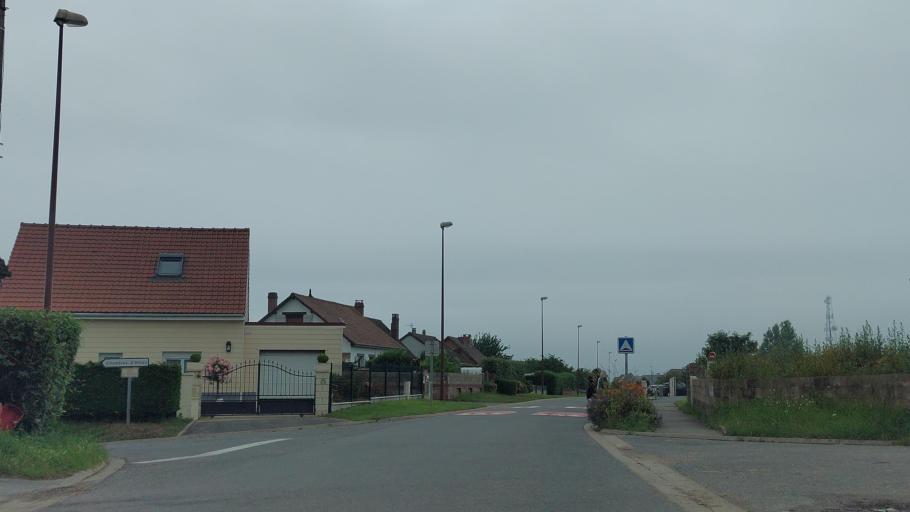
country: FR
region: Picardie
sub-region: Departement de la Somme
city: Ault
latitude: 50.0997
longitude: 1.4580
